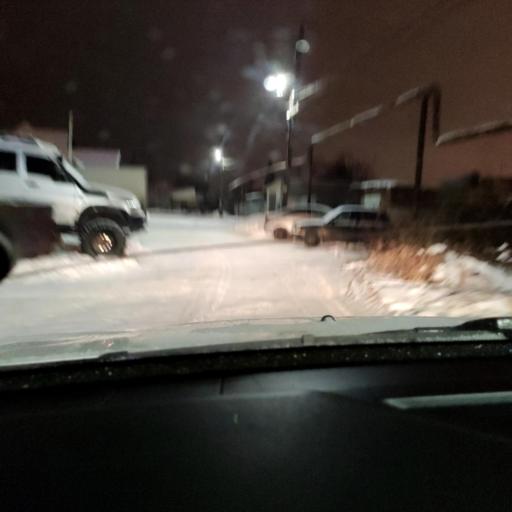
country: RU
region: Samara
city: Smyshlyayevka
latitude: 53.2405
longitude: 50.3223
